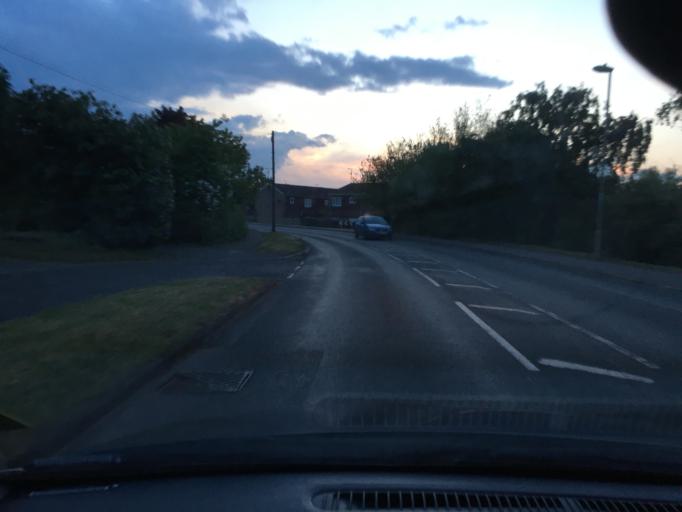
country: GB
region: England
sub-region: Bracknell Forest
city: Sandhurst
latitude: 51.3382
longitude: -0.7926
